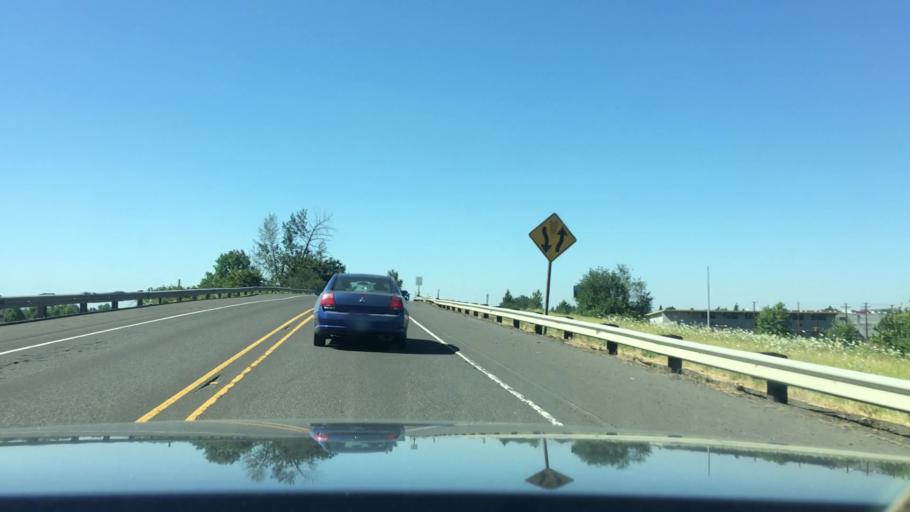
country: US
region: Oregon
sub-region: Lane County
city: Eugene
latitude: 44.0585
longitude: -123.1734
